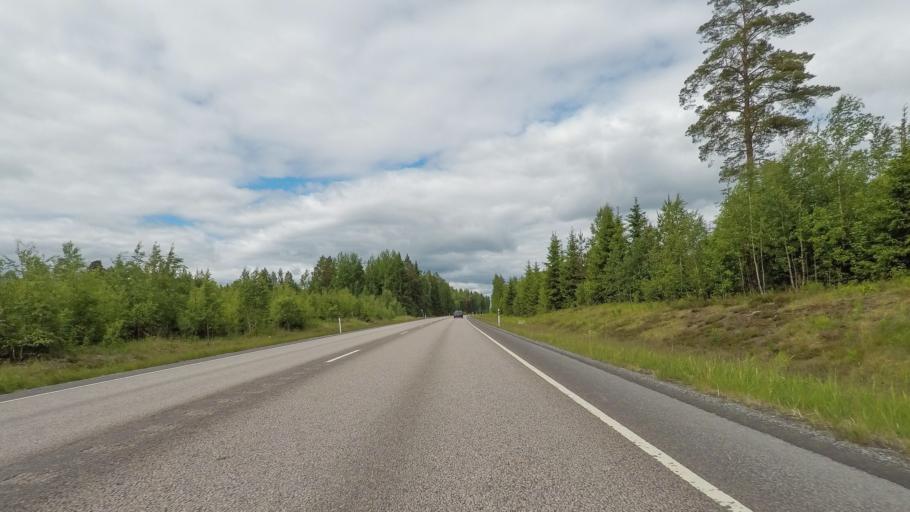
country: FI
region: Paijanne Tavastia
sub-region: Lahti
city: Hartola
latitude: 61.5923
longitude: 26.0086
